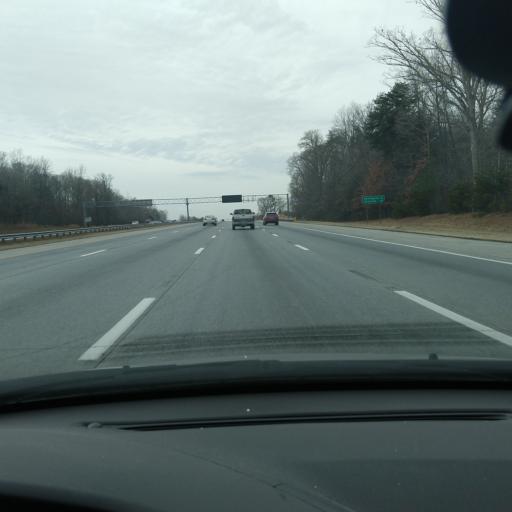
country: US
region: North Carolina
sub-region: Rowan County
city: Salisbury
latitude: 35.6251
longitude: -80.5014
